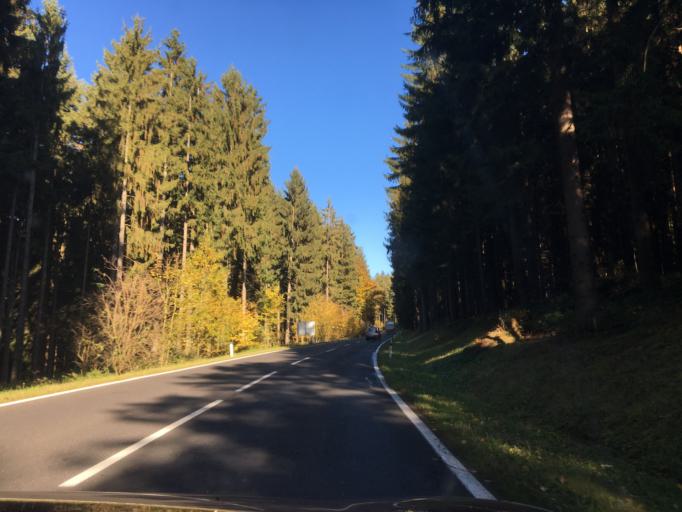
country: AT
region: Upper Austria
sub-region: Politischer Bezirk Freistadt
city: Freistadt
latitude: 48.4978
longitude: 14.6076
